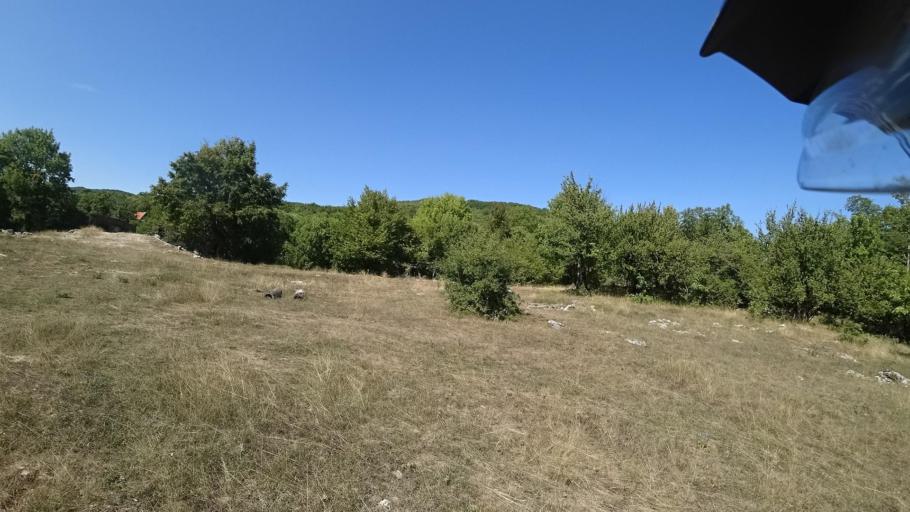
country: HR
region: Licko-Senjska
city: Otocac
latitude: 44.7338
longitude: 15.3529
